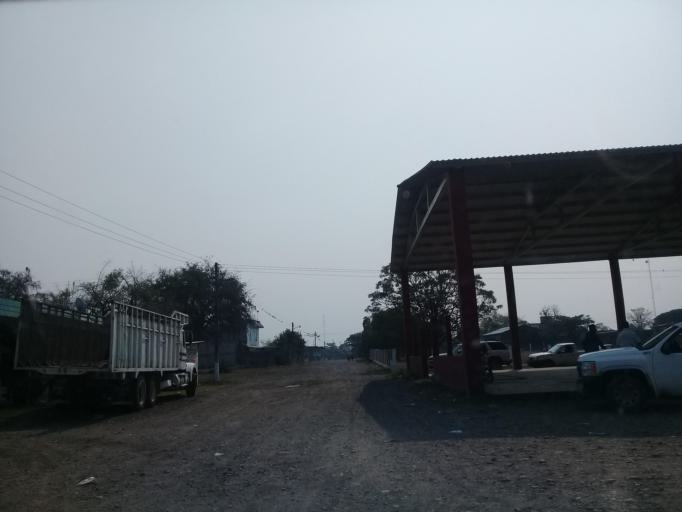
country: MX
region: Oaxaca
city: Acatlan de Perez Figueroa
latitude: 18.6064
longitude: -96.5777
